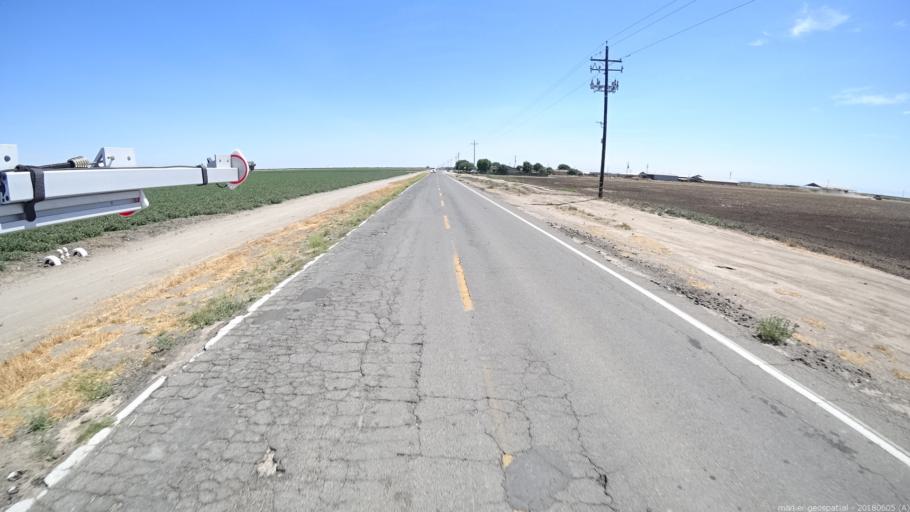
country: US
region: California
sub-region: Fresno County
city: Firebaugh
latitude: 36.9912
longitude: -120.3832
